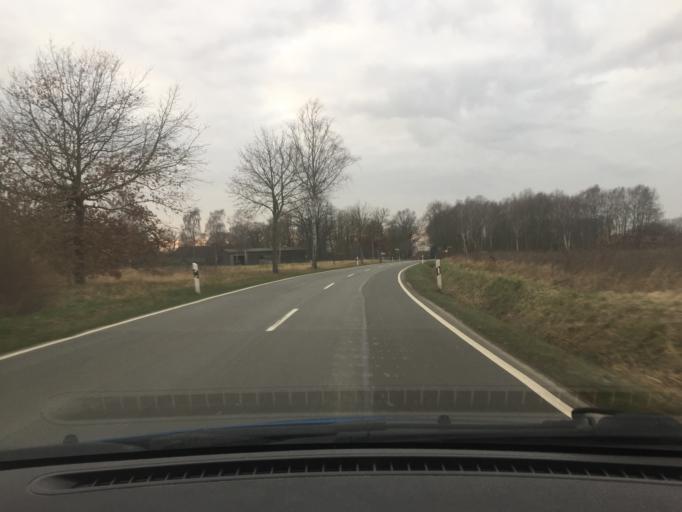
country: DE
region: Lower Saxony
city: Oetzen
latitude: 53.0408
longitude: 10.6531
